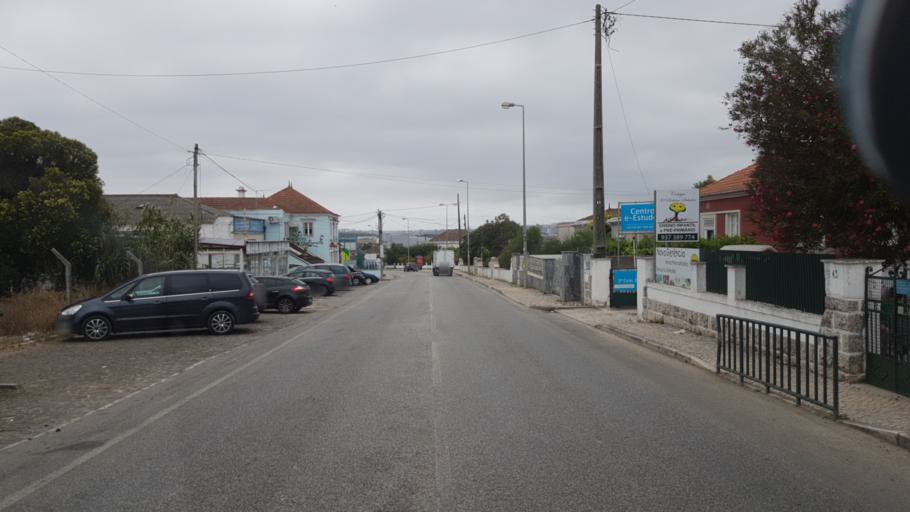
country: PT
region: Lisbon
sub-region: Sintra
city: Pero Pinheiro
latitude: 38.8538
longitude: -9.3263
